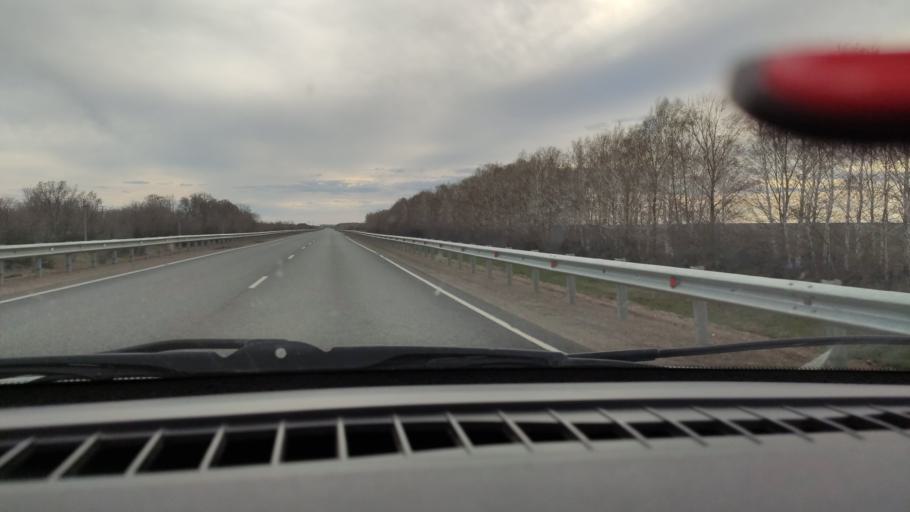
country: RU
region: Bashkortostan
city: Mayachnyy
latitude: 52.4052
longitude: 55.7268
